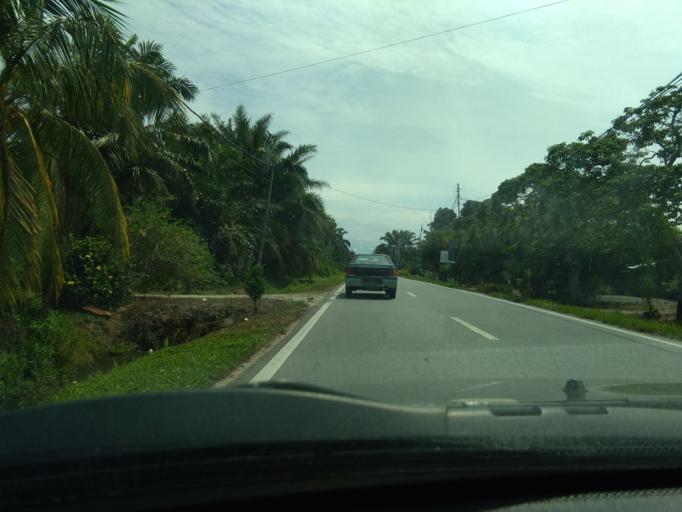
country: MY
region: Perak
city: Bagan Serai
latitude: 5.0403
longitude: 100.5732
